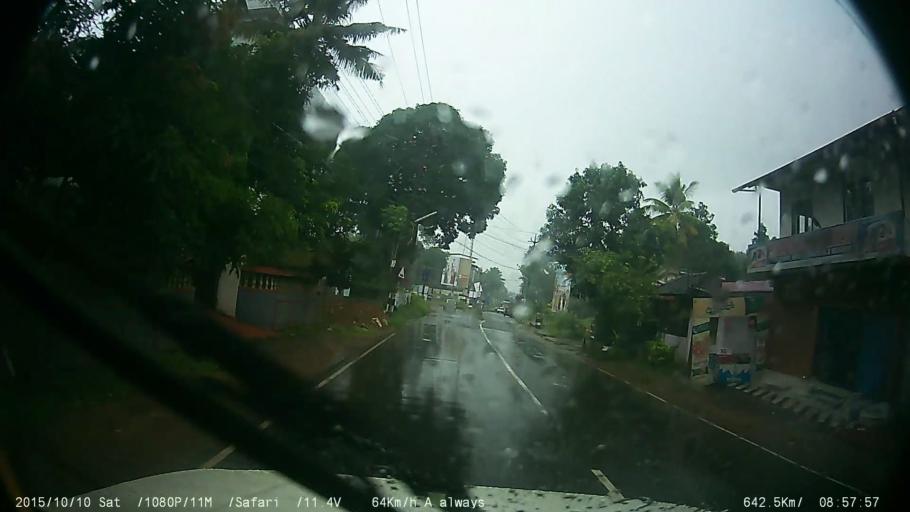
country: IN
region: Kerala
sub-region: Kottayam
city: Palackattumala
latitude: 9.6864
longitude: 76.5564
